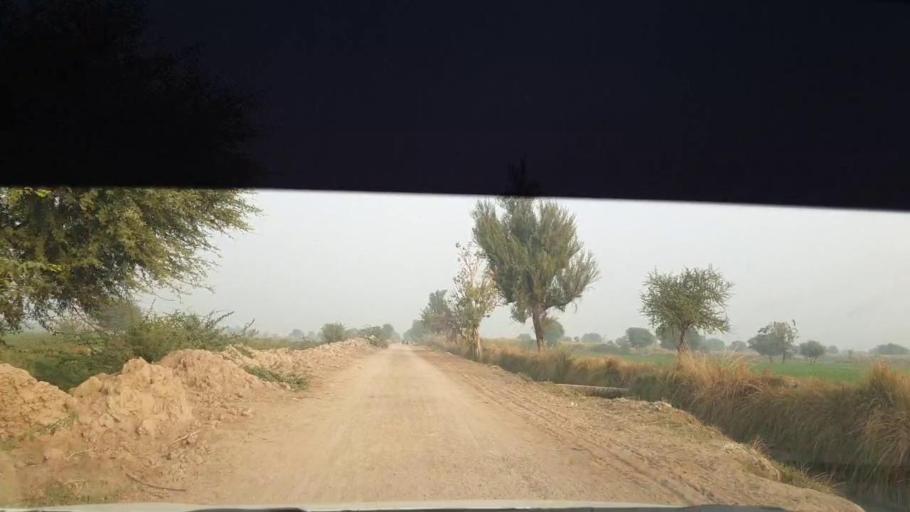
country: PK
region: Sindh
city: Berani
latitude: 25.8421
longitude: 68.8914
